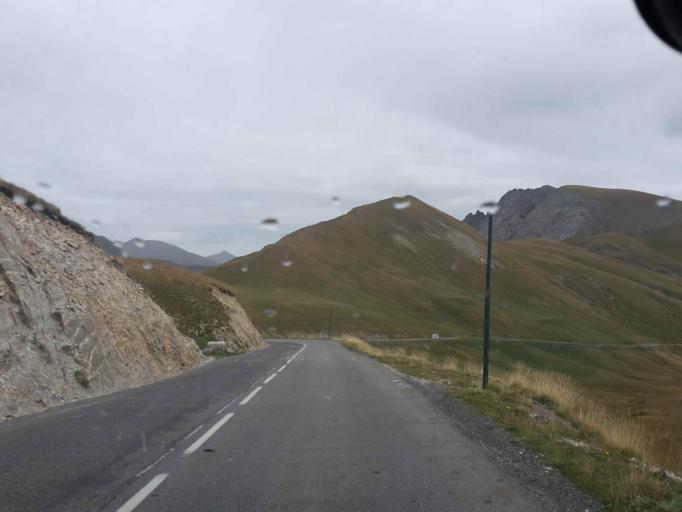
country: FR
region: Rhone-Alpes
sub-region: Departement de la Savoie
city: Valloire
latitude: 45.0744
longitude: 6.4134
